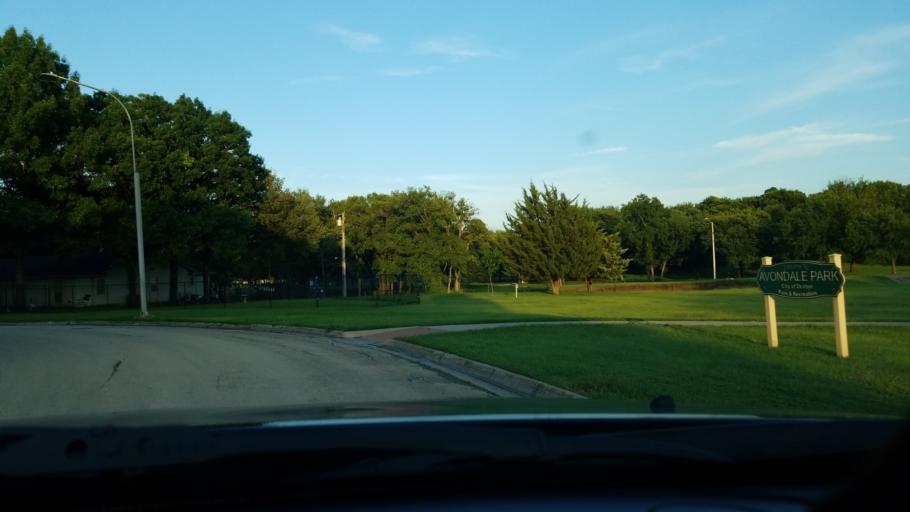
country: US
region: Texas
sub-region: Denton County
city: Denton
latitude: 33.2438
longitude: -97.1097
